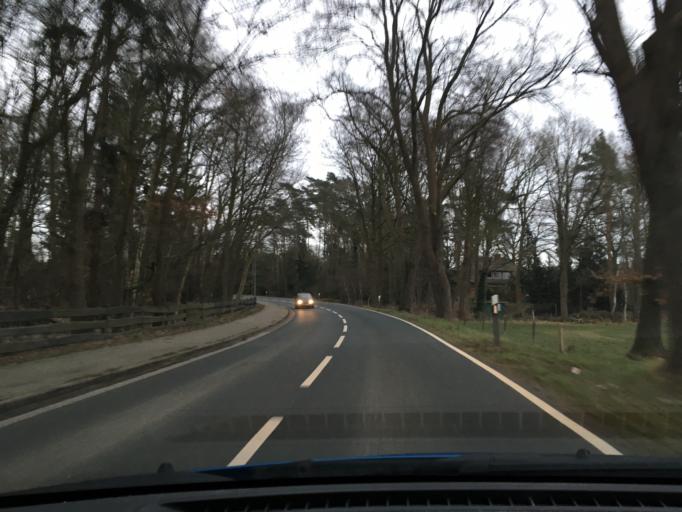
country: DE
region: Lower Saxony
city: Wittorf
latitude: 53.3331
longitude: 10.3936
